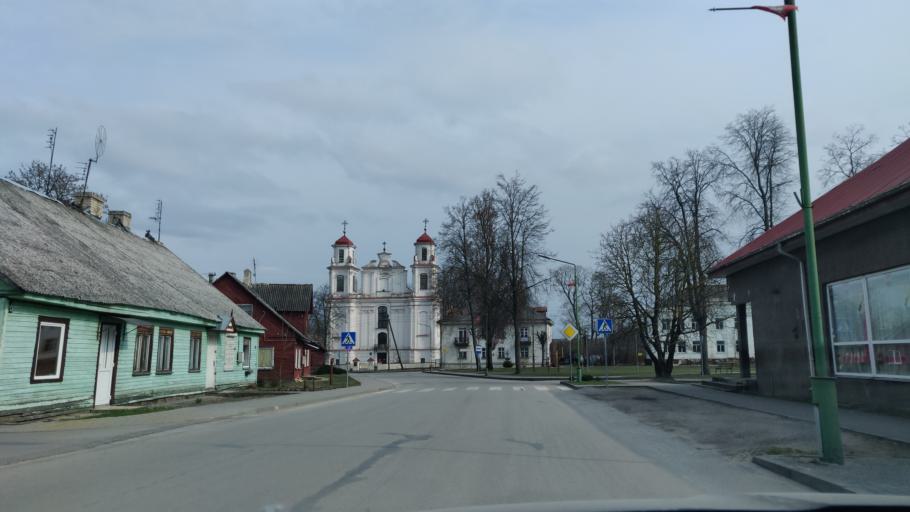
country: LT
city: Jieznas
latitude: 54.5994
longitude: 24.1714
